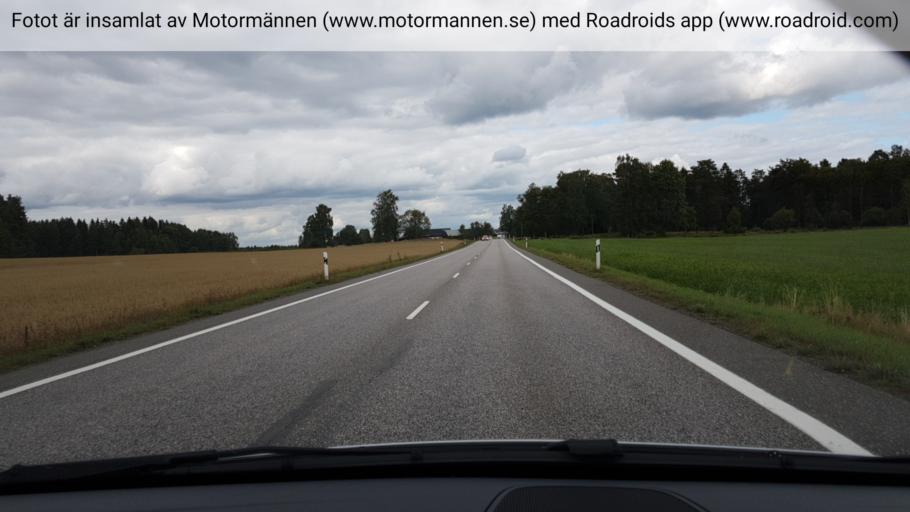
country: SE
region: Vaestra Goetaland
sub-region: Tidaholms Kommun
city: Tidaholm
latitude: 58.1518
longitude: 13.9209
